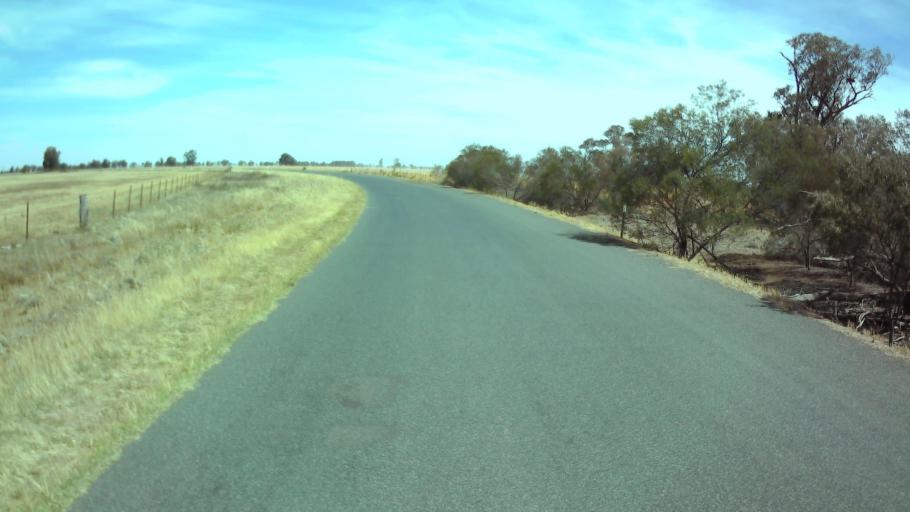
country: AU
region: New South Wales
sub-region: Weddin
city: Grenfell
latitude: -33.9373
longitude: 147.7614
